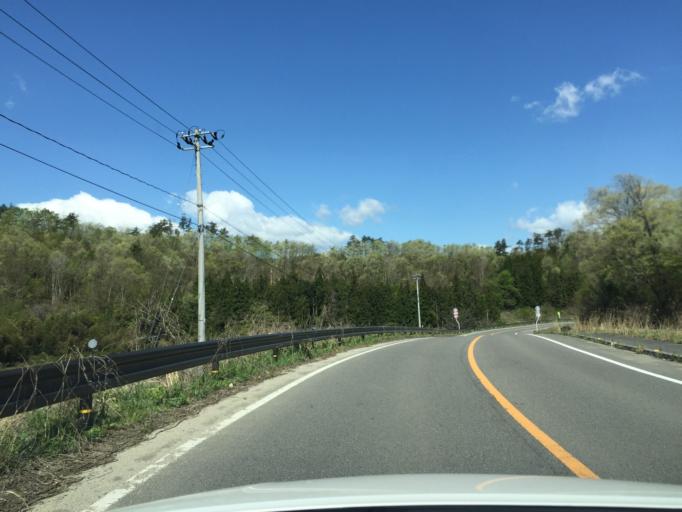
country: JP
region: Fukushima
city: Funehikimachi-funehiki
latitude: 37.5369
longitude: 140.5372
